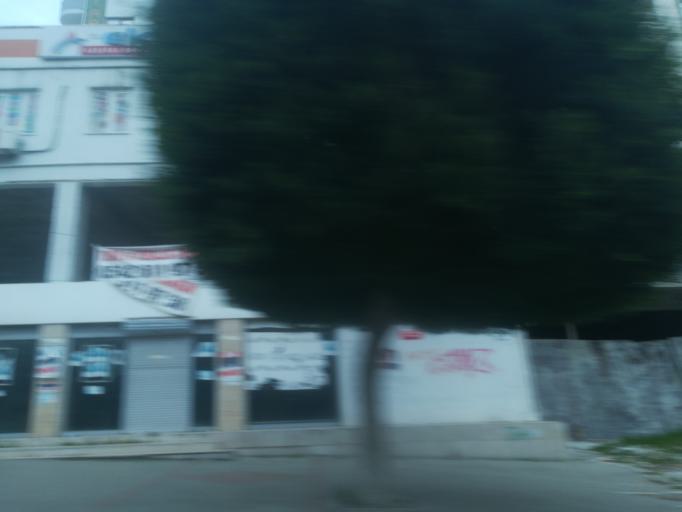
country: TR
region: Adana
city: Adana
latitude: 37.0404
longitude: 35.2926
